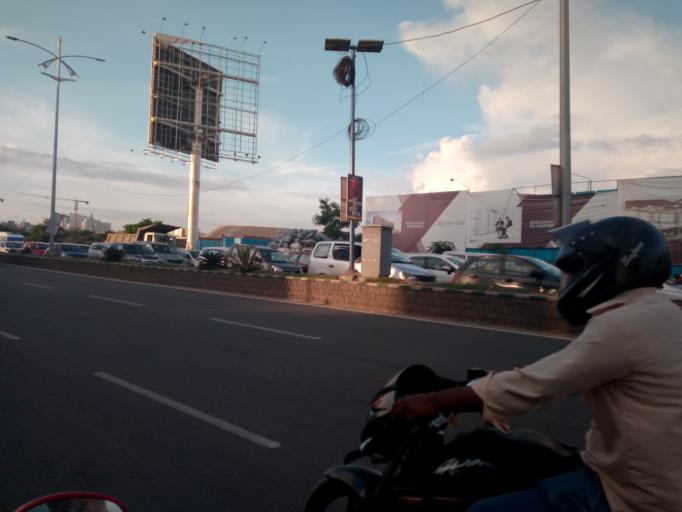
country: IN
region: Telangana
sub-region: Rangareddi
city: Kukatpalli
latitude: 17.4331
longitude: 78.3746
